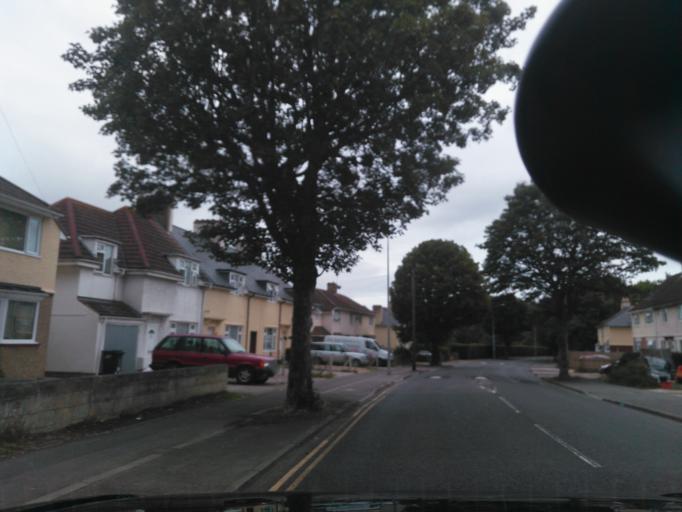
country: GB
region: England
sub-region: Borough of Swindon
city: Swindon
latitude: 51.5744
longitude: -1.7867
